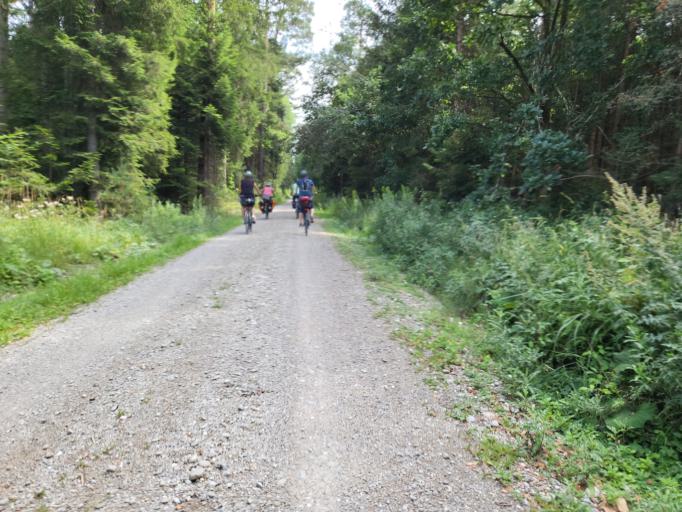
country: DE
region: Bavaria
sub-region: Upper Bavaria
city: Hohenkirchen-Siegertsbrunn
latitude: 48.0317
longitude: 11.7487
